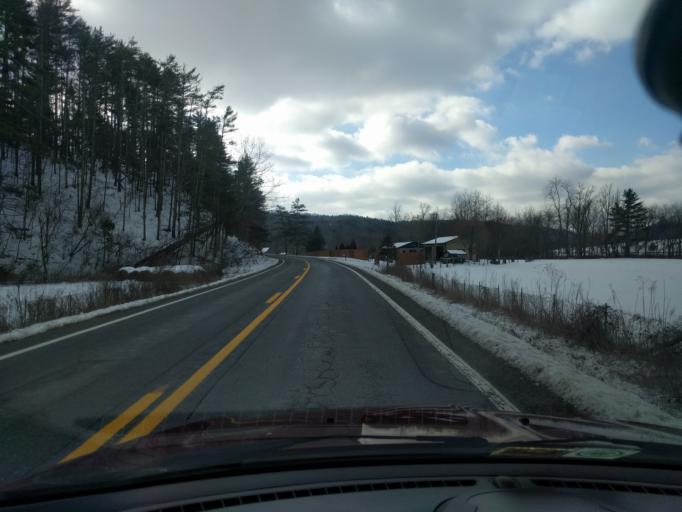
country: US
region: West Virginia
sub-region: Pocahontas County
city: Marlinton
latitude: 38.1510
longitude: -79.9832
